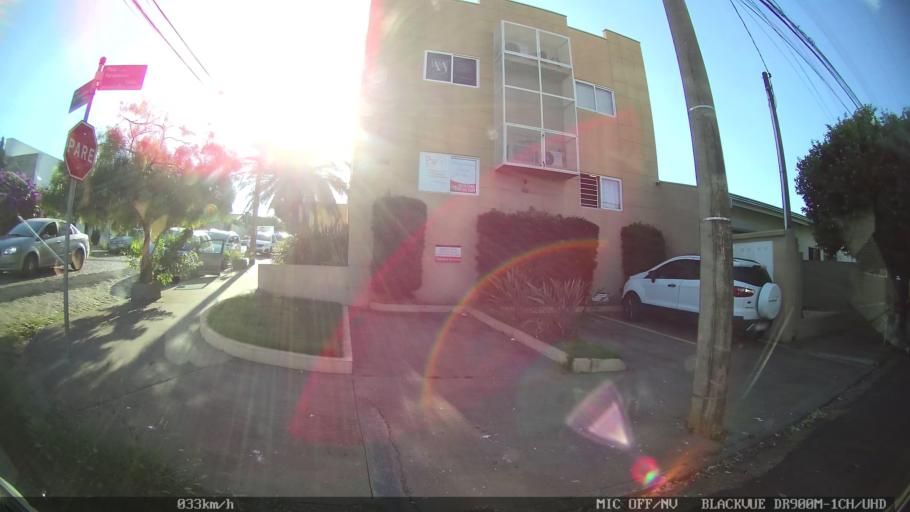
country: BR
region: Sao Paulo
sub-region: Sao Jose Do Rio Preto
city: Sao Jose do Rio Preto
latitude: -20.8206
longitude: -49.4001
